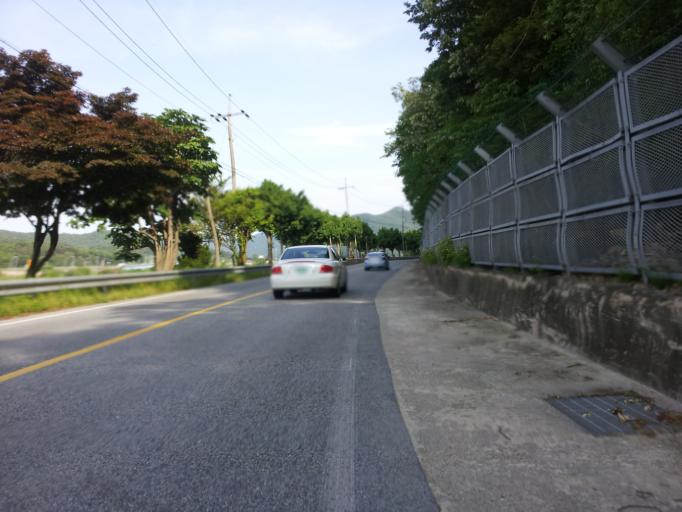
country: KR
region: Chungcheongnam-do
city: Gongju
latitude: 36.4422
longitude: 127.1917
